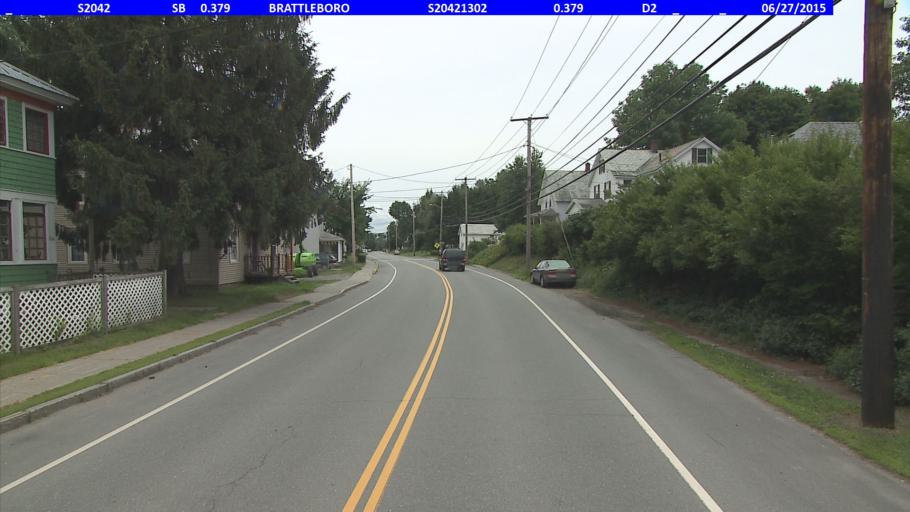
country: US
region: Vermont
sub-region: Windham County
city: Brattleboro
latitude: 42.8427
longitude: -72.5568
